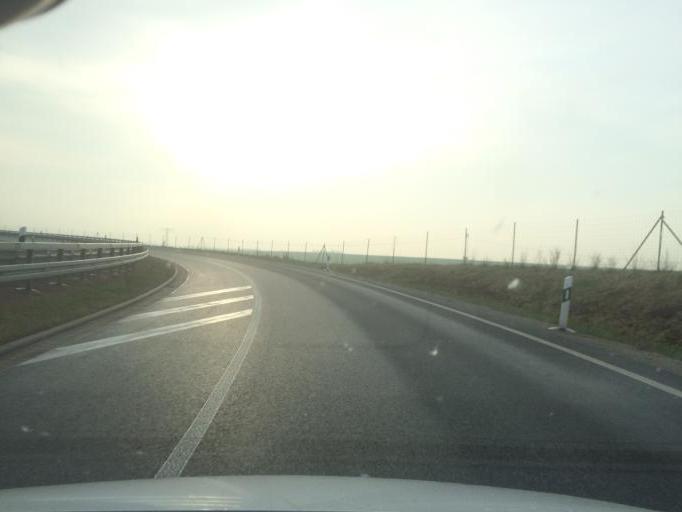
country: DE
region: Thuringia
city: Nohra
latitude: 51.4883
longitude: 10.7188
